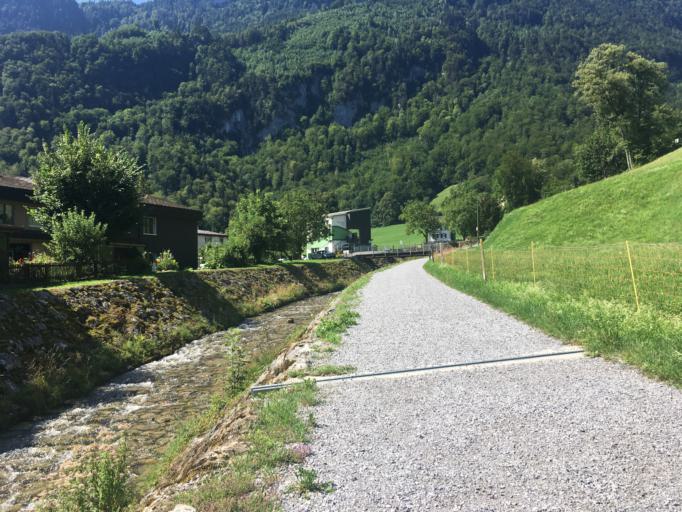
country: CH
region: Glarus
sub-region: Glarus
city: Niederurnen
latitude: 47.1256
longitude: 9.0477
